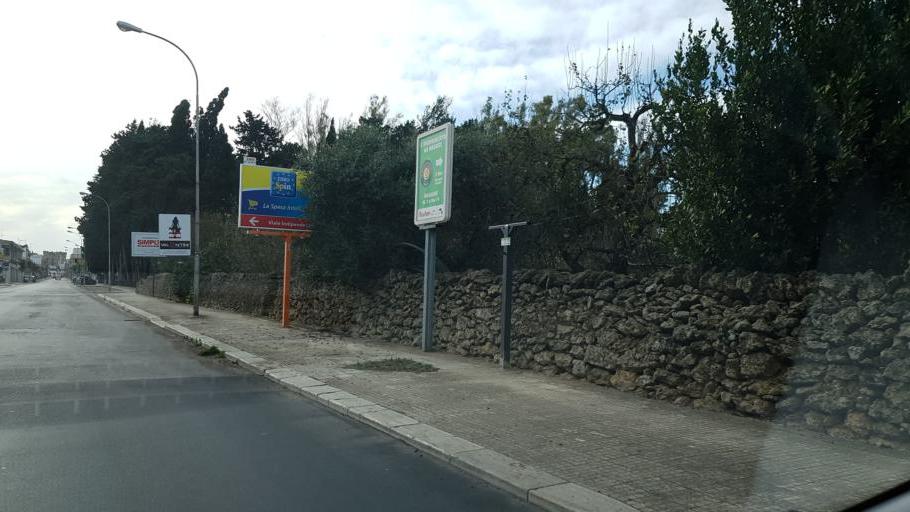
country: IT
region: Apulia
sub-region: Provincia di Brindisi
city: Mesagne
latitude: 40.5648
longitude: 17.8148
